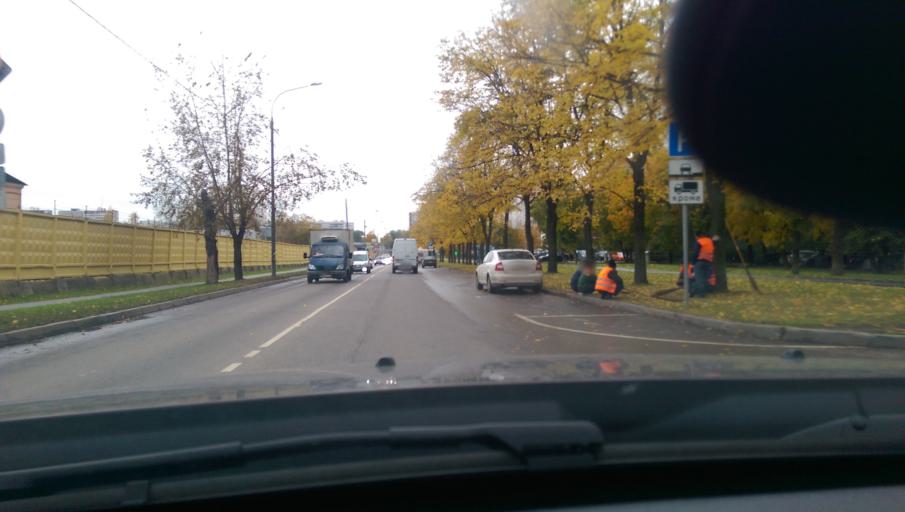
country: RU
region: Moscow
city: Altuf'yevskiy
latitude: 55.8912
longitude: 37.5769
